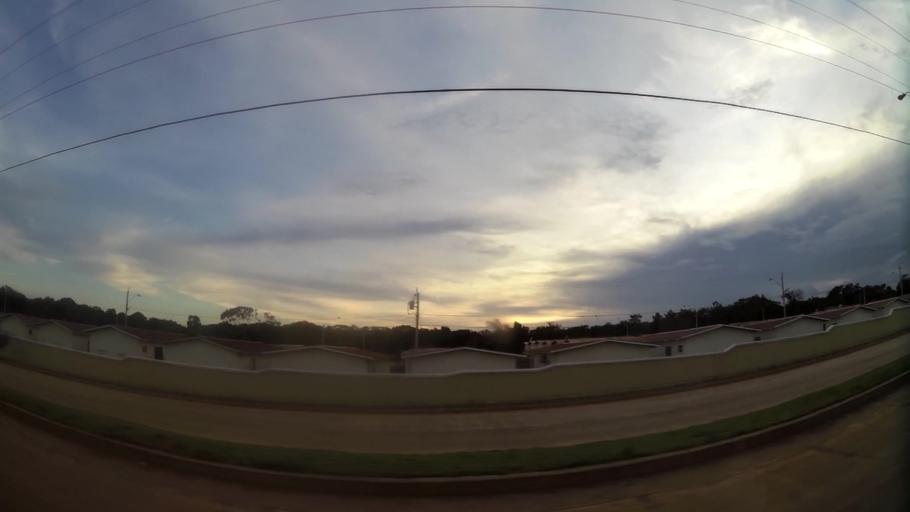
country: PA
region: Panama
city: La Mitra
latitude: 8.8569
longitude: -79.7587
